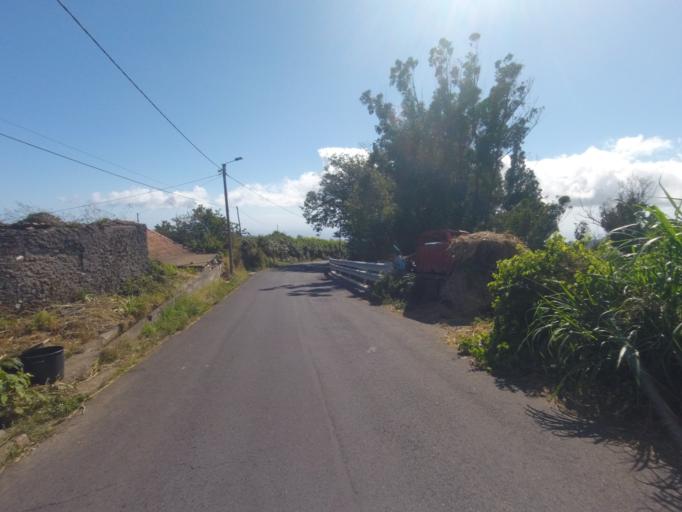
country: PT
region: Madeira
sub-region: Ribeira Brava
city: Campanario
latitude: 32.6996
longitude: -17.0234
